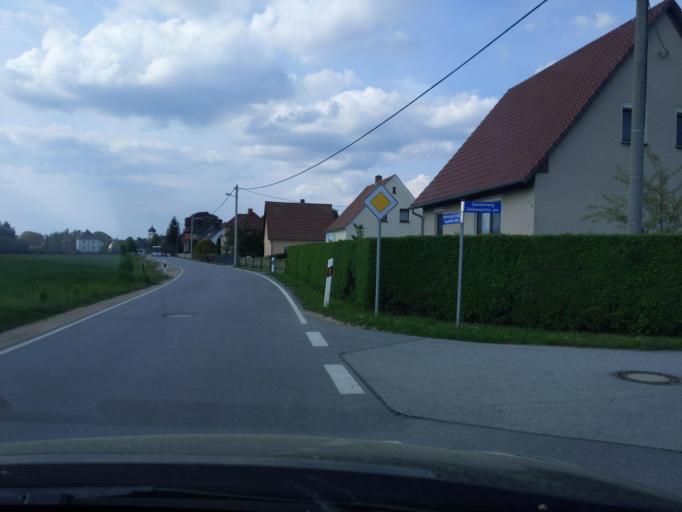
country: DE
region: Saxony
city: Malschwitz
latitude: 51.2333
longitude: 14.5241
